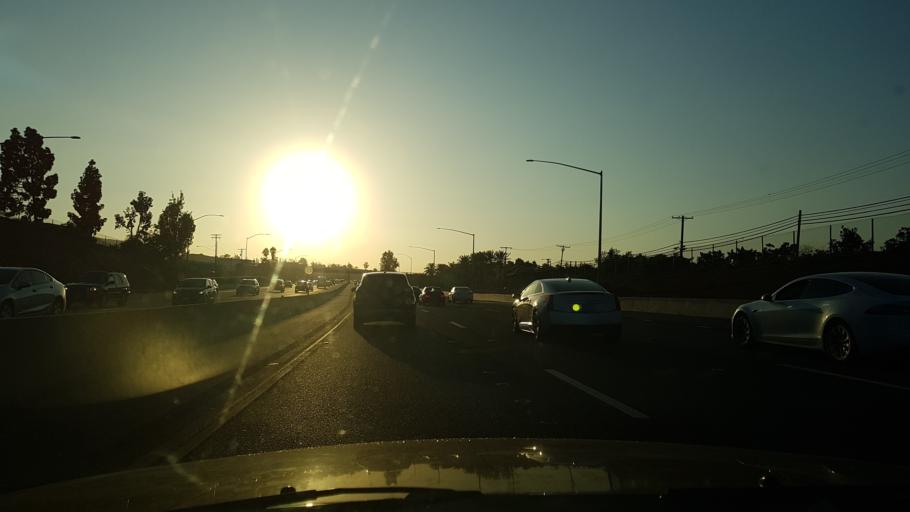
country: US
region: California
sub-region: San Diego County
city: San Marcos
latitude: 33.1394
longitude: -117.1530
